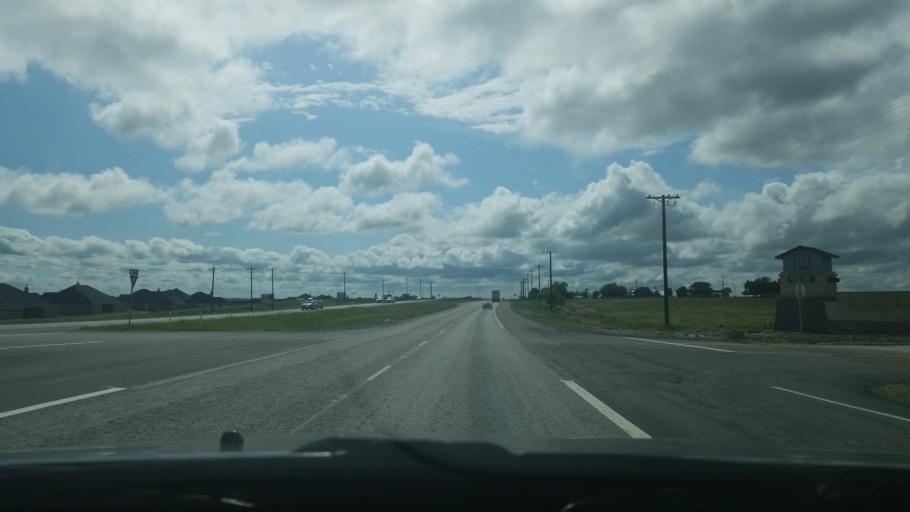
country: US
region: Texas
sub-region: Denton County
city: Ponder
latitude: 33.2417
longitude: -97.3620
